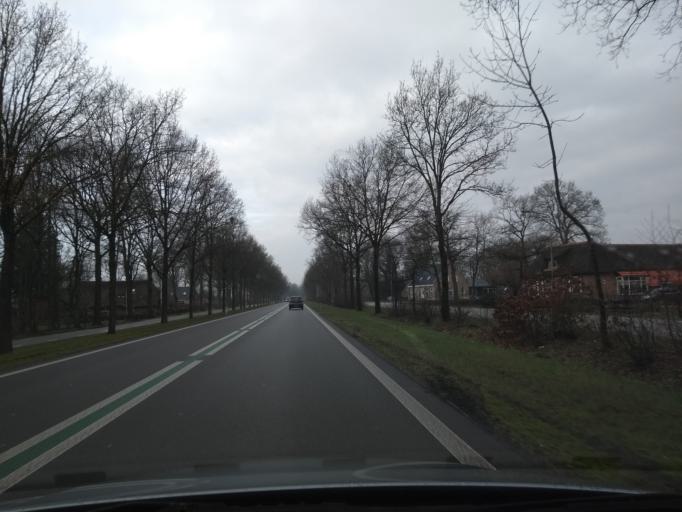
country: NL
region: Overijssel
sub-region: Gemeente Dalfsen
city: Dalfsen
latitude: 52.5917
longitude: 6.3067
